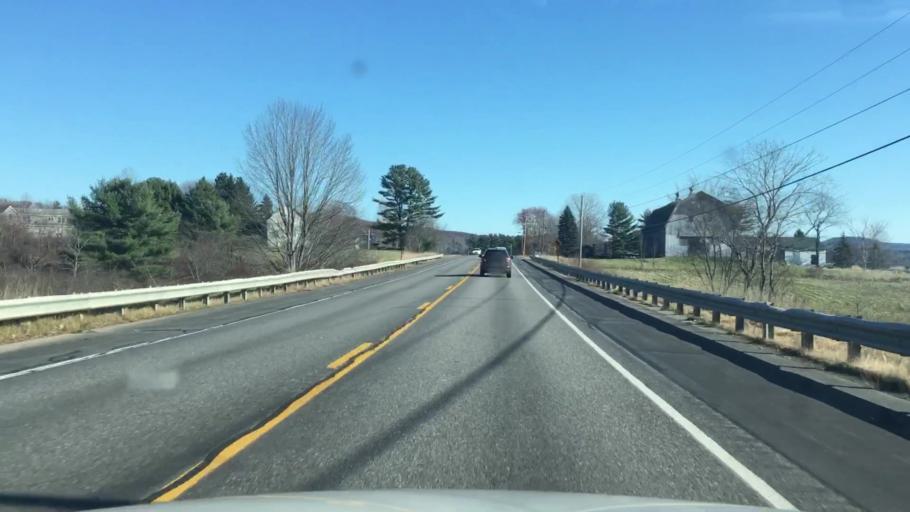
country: US
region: Maine
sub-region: Knox County
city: Union
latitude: 44.2162
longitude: -69.2996
